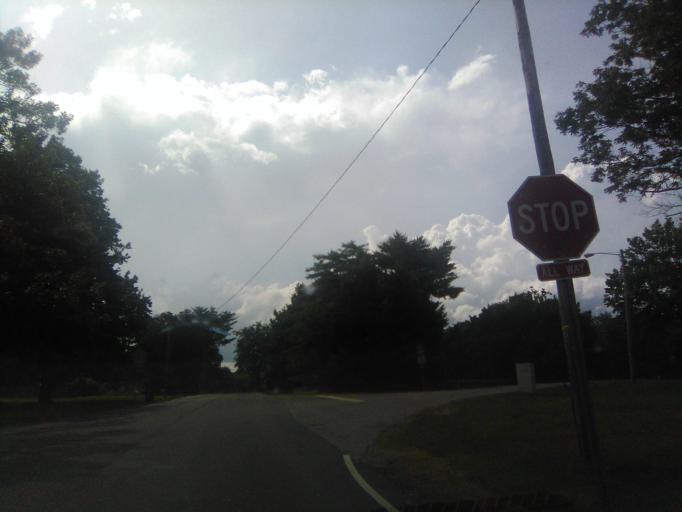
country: US
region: Tennessee
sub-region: Davidson County
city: Belle Meade
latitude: 36.0955
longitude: -86.8691
